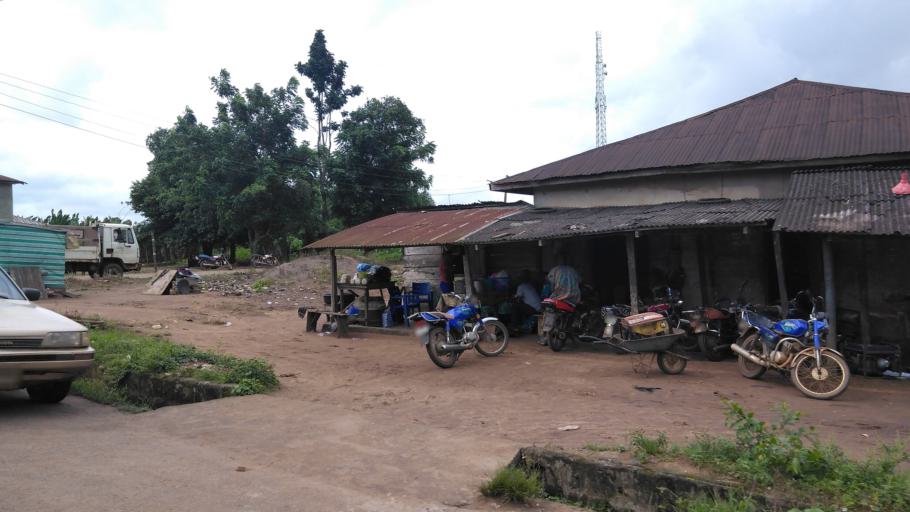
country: NG
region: Ogun
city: Abigi
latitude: 6.6011
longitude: 4.4911
